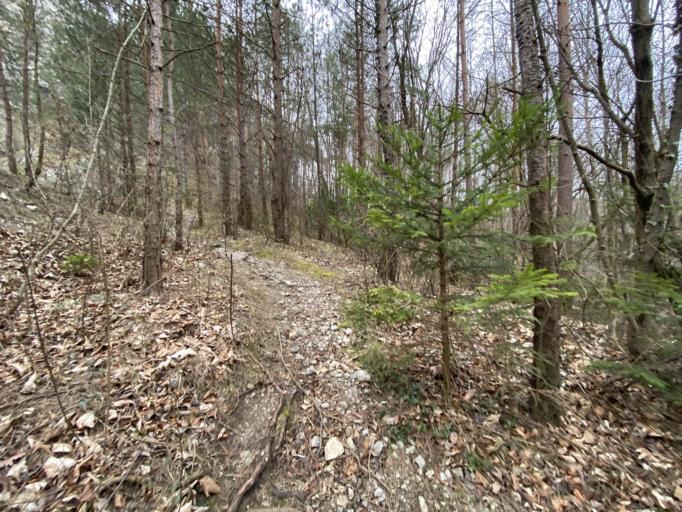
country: AT
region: Lower Austria
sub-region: Politischer Bezirk Modling
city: Gaaden
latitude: 48.0226
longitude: 16.1912
